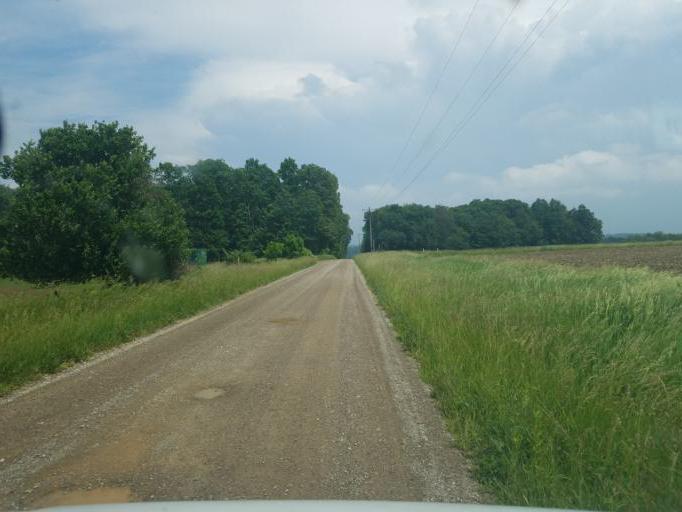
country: US
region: Ohio
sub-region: Knox County
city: Oak Hill
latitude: 40.3566
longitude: -82.2661
